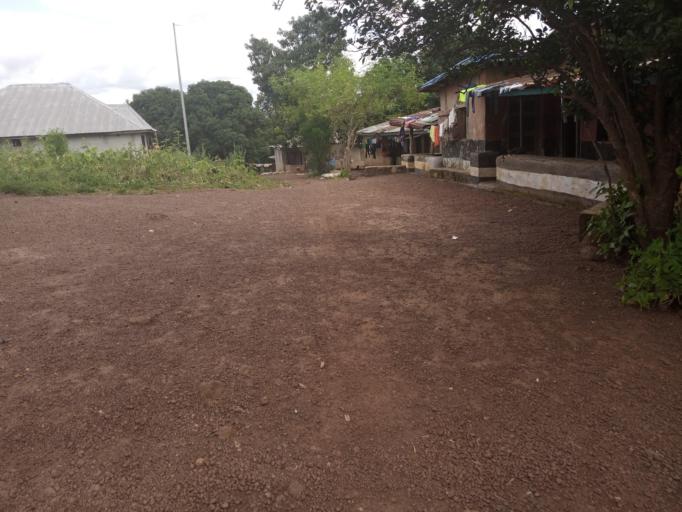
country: SL
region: Northern Province
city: Kamakwie
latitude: 9.4936
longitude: -12.2400
